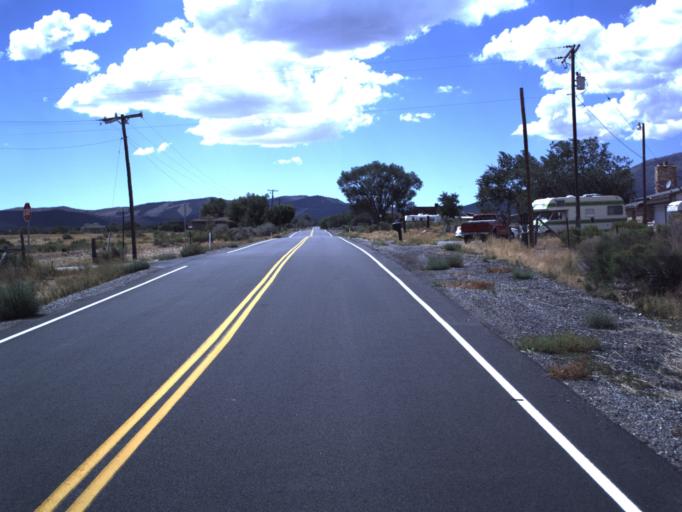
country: US
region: Utah
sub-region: Tooele County
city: Tooele
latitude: 40.3388
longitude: -112.4646
